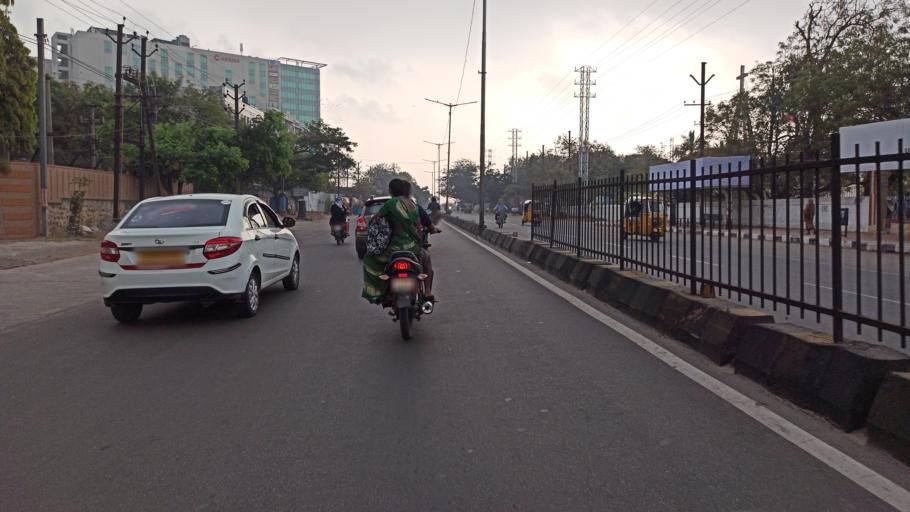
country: IN
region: Telangana
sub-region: Rangareddi
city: Uppal Kalan
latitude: 17.4010
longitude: 78.5437
